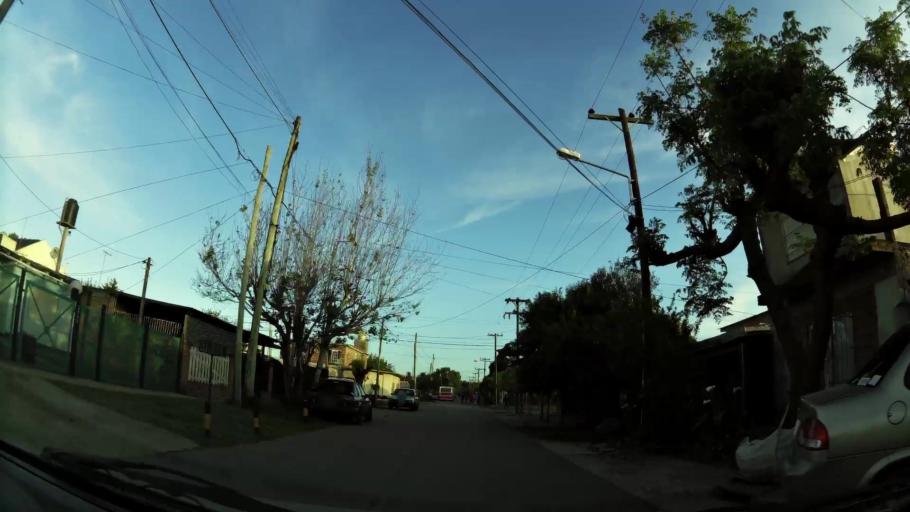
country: AR
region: Buenos Aires
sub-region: Partido de Quilmes
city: Quilmes
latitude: -34.7852
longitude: -58.2172
